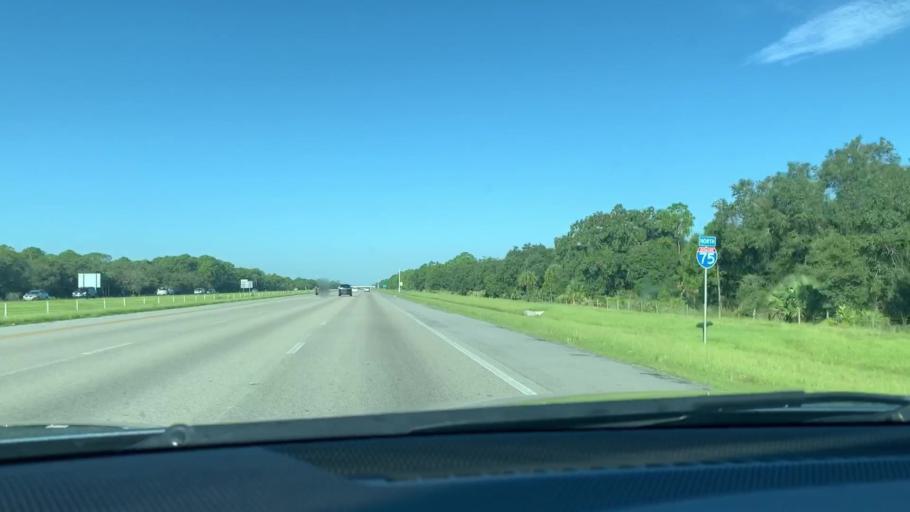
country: US
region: Florida
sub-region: Sarasota County
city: North Port
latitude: 27.0999
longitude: -82.2117
